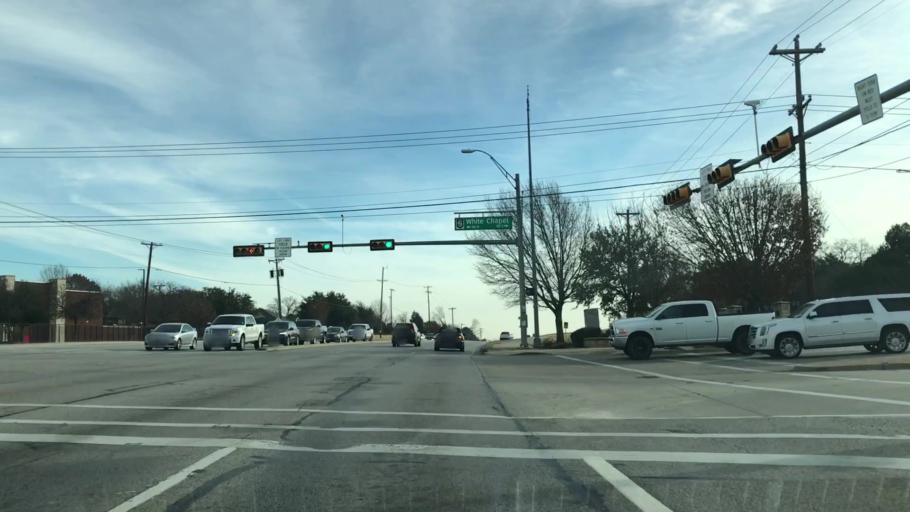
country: US
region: Texas
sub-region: Tarrant County
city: Southlake
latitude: 32.9414
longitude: -97.1513
